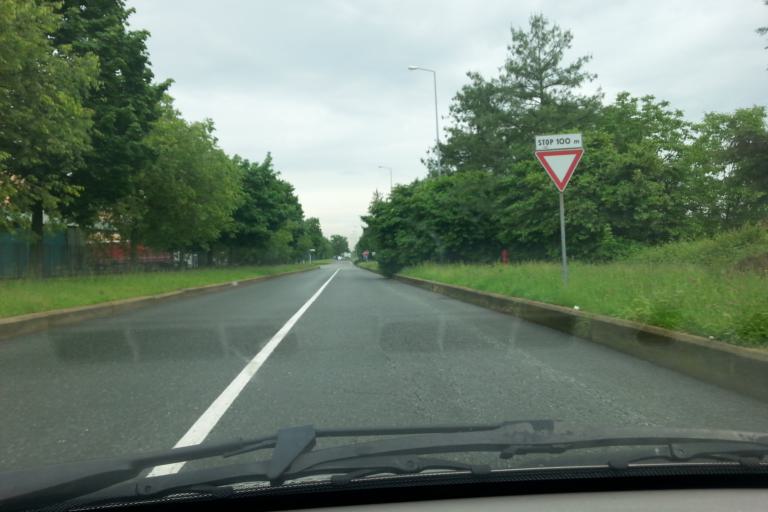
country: IT
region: Piedmont
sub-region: Provincia di Torino
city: Pasta
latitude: 45.0344
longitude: 7.5579
